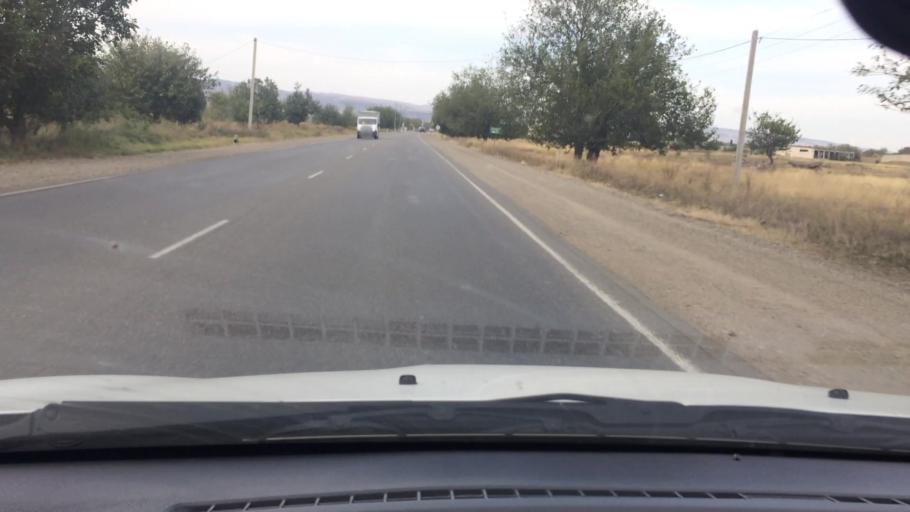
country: GE
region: Kvemo Kartli
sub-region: Marneuli
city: Marneuli
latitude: 41.5671
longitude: 44.7755
